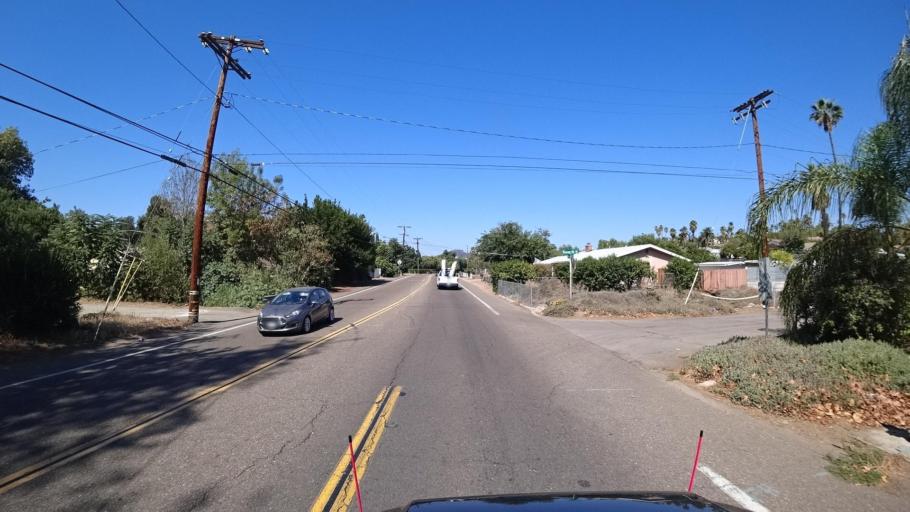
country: US
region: California
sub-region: San Diego County
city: Granite Hills
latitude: 32.8079
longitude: -116.9114
